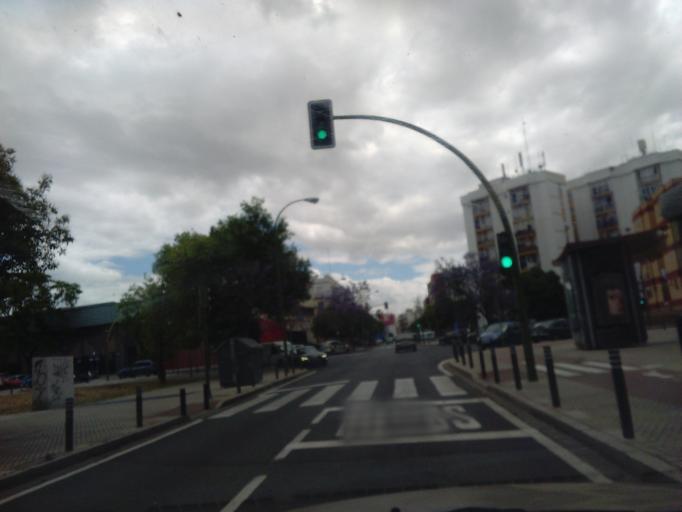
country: ES
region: Andalusia
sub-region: Provincia de Sevilla
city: Sevilla
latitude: 37.3734
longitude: -5.9528
